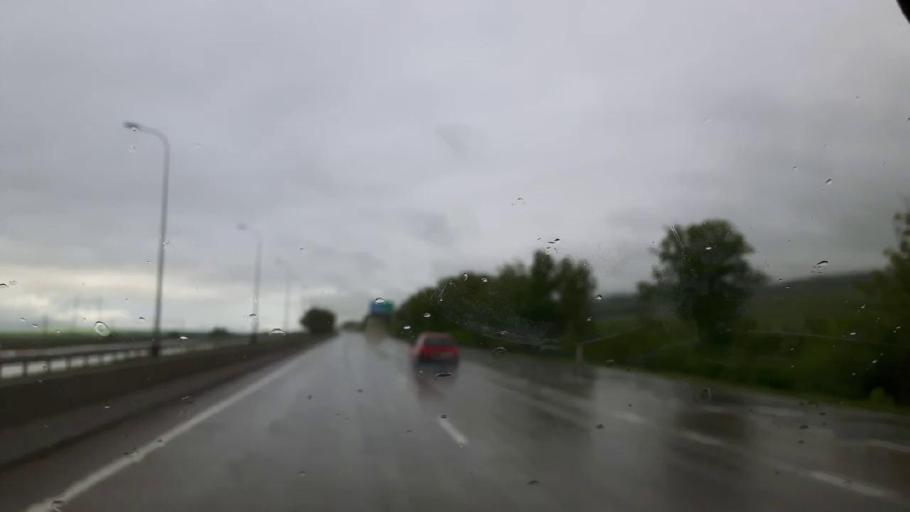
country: GE
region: Shida Kartli
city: Kaspi
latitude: 42.0144
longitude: 44.3246
